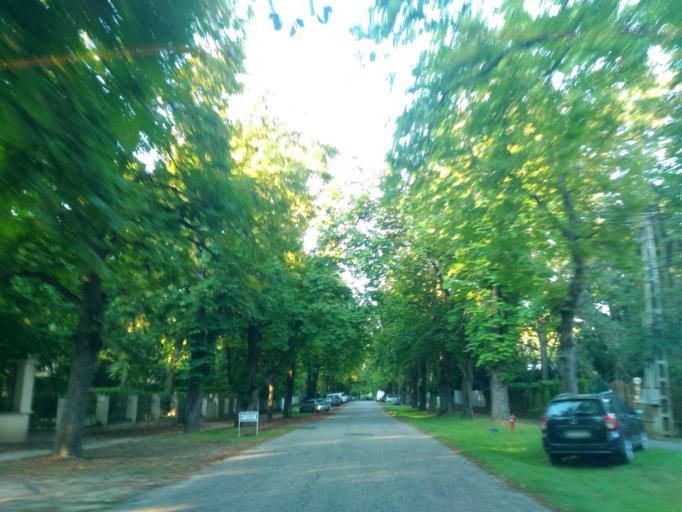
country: HU
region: Somogy
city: Balatonszarszo
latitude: 46.8124
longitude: 17.7807
